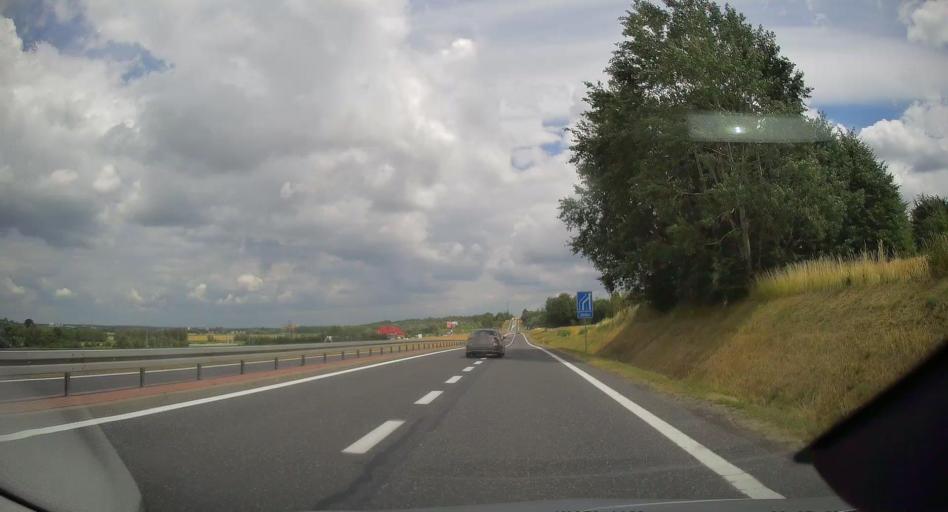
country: PL
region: Subcarpathian Voivodeship
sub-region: Powiat ropczycko-sedziszowski
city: Ostrow
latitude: 50.0618
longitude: 21.5556
